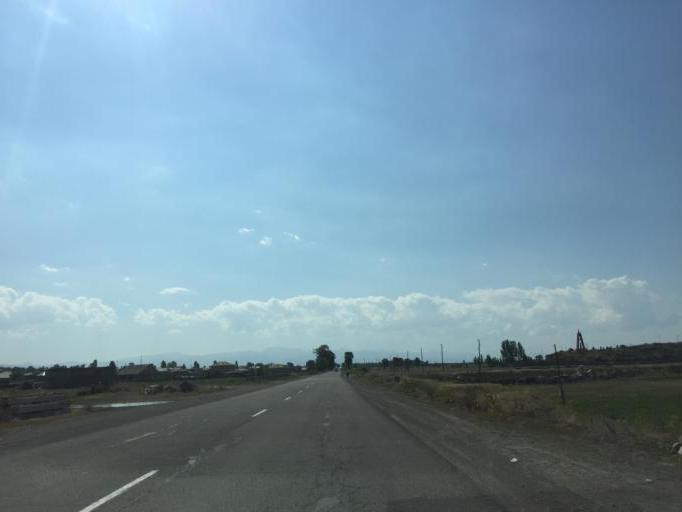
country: AM
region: Geghark'unik'i Marz
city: Tsovinar
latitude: 40.1624
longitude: 45.4769
